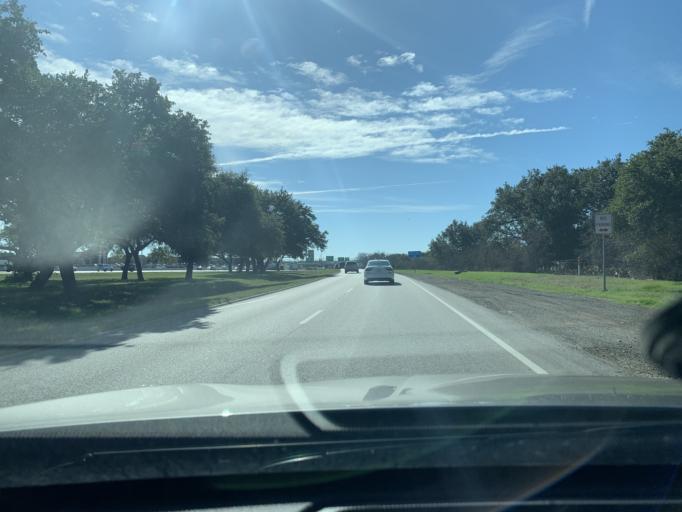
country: US
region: Texas
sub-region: Williamson County
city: Round Rock
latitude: 30.5636
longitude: -97.6934
